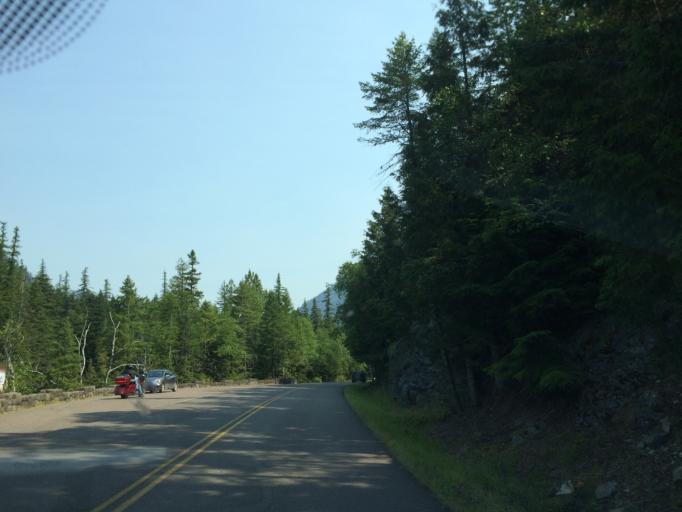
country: US
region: Montana
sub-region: Flathead County
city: Columbia Falls
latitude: 48.6575
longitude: -113.8391
